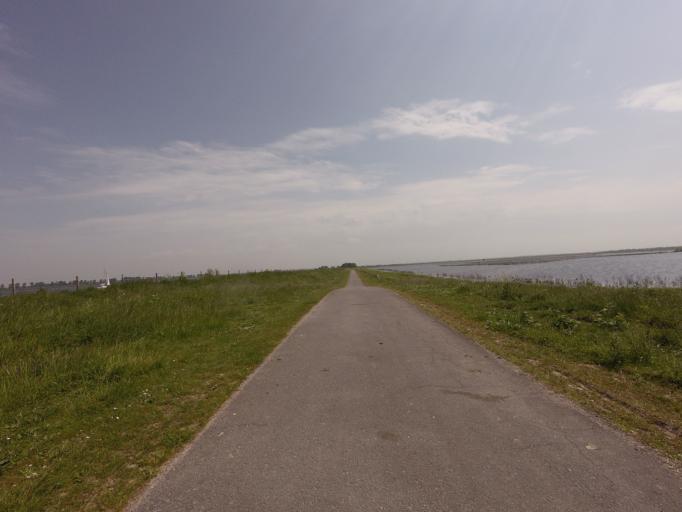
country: NL
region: South Holland
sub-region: Gemeente Spijkenisse
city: Spijkenisse
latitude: 51.7431
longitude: 4.3236
